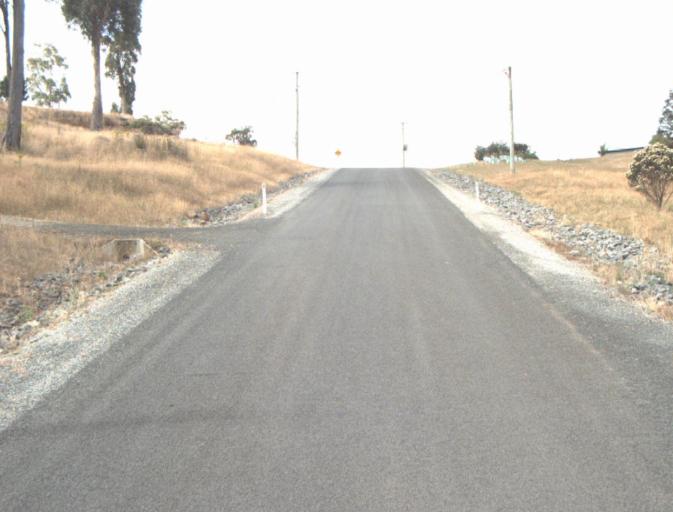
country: AU
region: Tasmania
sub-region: Launceston
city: Mayfield
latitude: -41.3006
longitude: 147.0440
